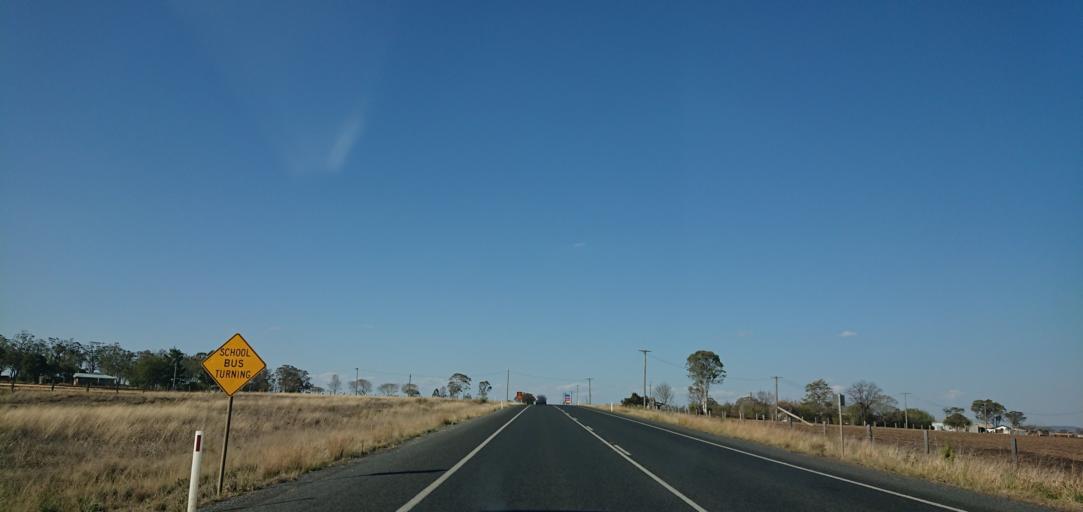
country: AU
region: Queensland
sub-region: Toowoomba
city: Westbrook
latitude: -27.6399
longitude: 151.7388
